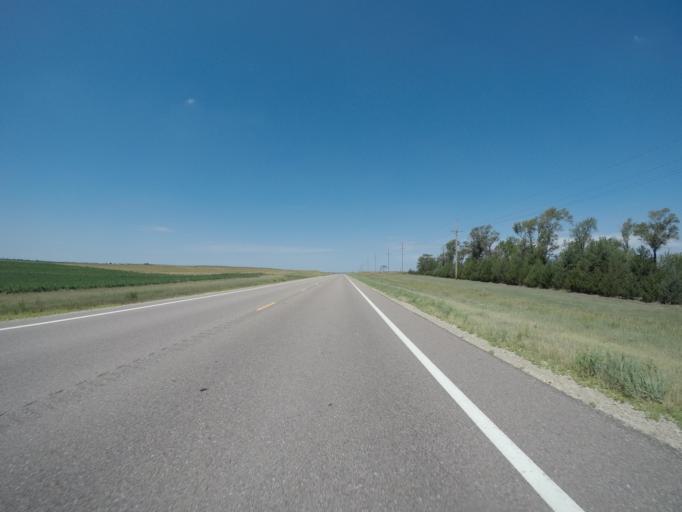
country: US
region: Kansas
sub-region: Osborne County
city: Osborne
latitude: 39.5099
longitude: -98.6640
